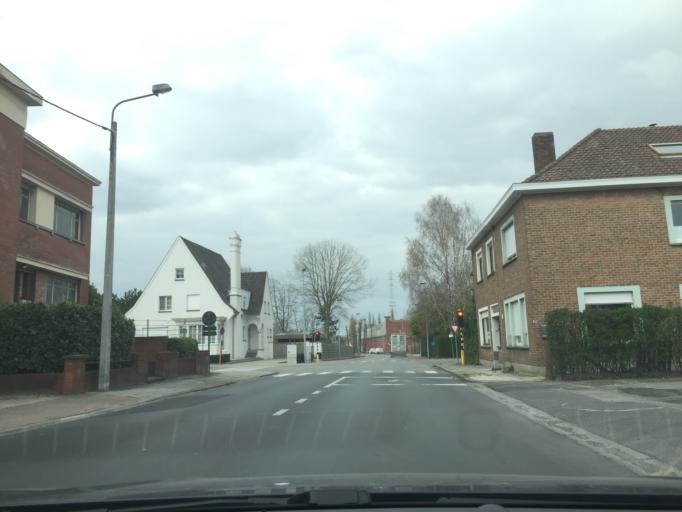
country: BE
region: Flanders
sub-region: Provincie West-Vlaanderen
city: Zwevegem
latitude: 50.8187
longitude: 3.3407
